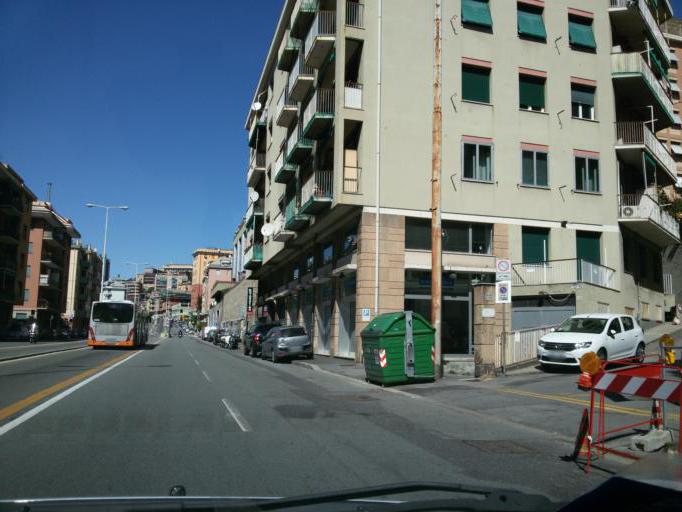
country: IT
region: Liguria
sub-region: Provincia di Genova
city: Genoa
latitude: 44.4042
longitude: 8.9823
